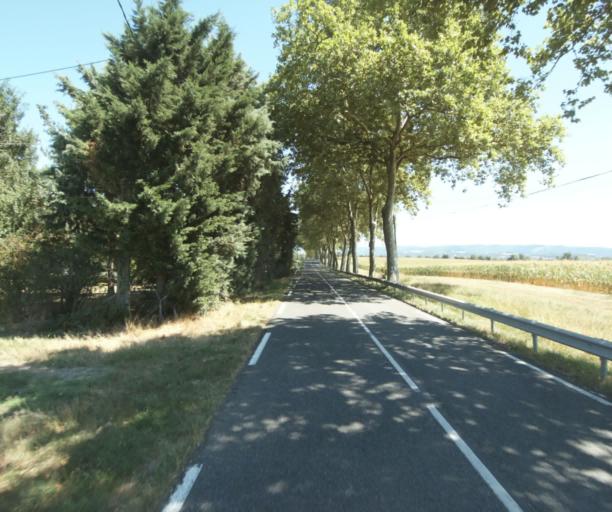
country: FR
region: Midi-Pyrenees
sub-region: Departement de la Haute-Garonne
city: Saint-Felix-Lauragais
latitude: 43.4731
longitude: 1.9427
